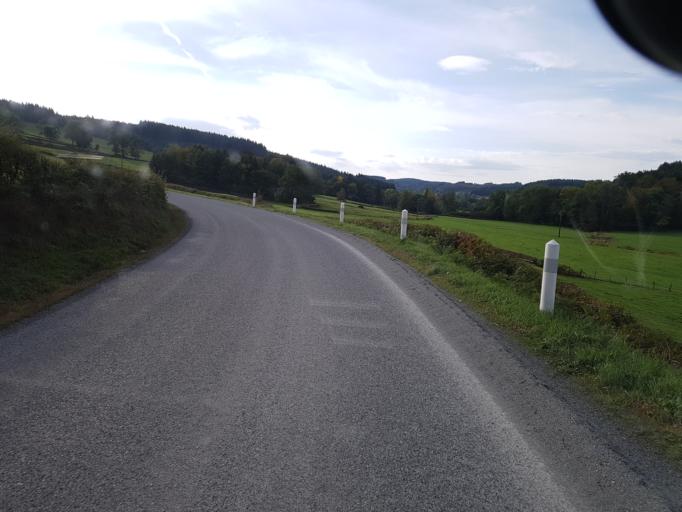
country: FR
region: Bourgogne
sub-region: Departement de Saone-et-Loire
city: Chauffailles
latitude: 46.2612
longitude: 4.4005
